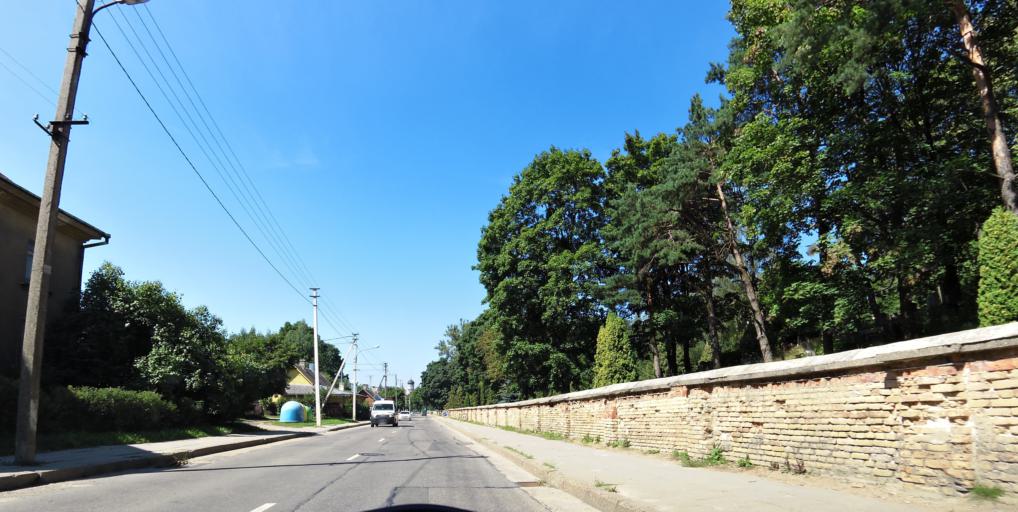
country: LT
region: Vilnius County
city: Rasos
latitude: 54.6634
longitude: 25.2970
